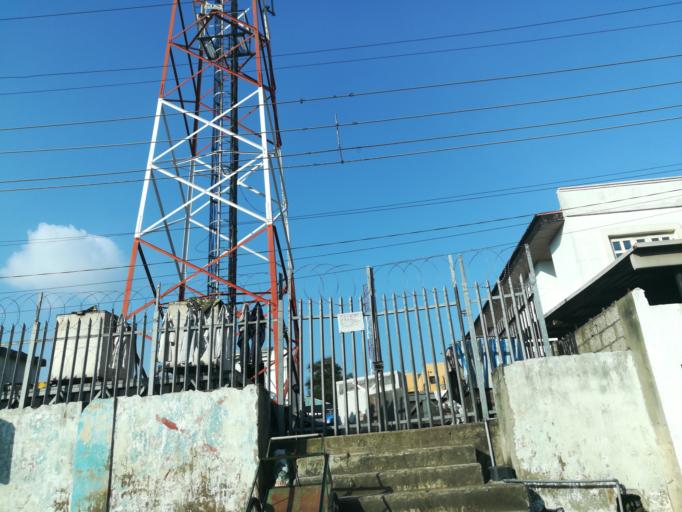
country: NG
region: Lagos
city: Ojota
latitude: 6.5872
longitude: 3.3643
